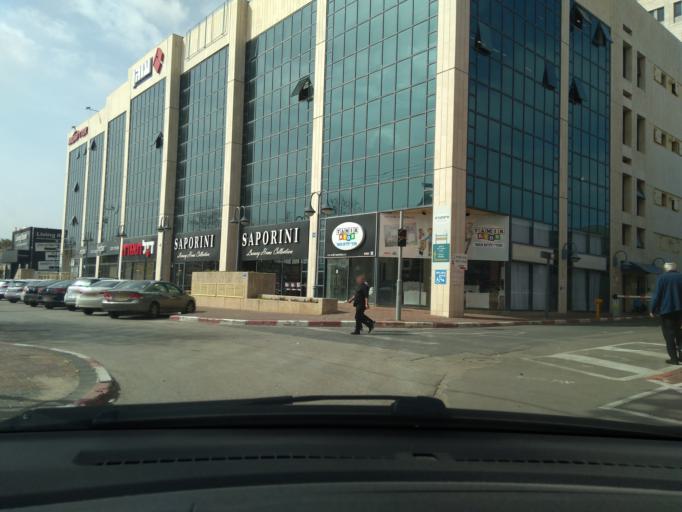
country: IL
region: Central District
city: Even Yehuda
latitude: 32.2774
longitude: 34.8598
